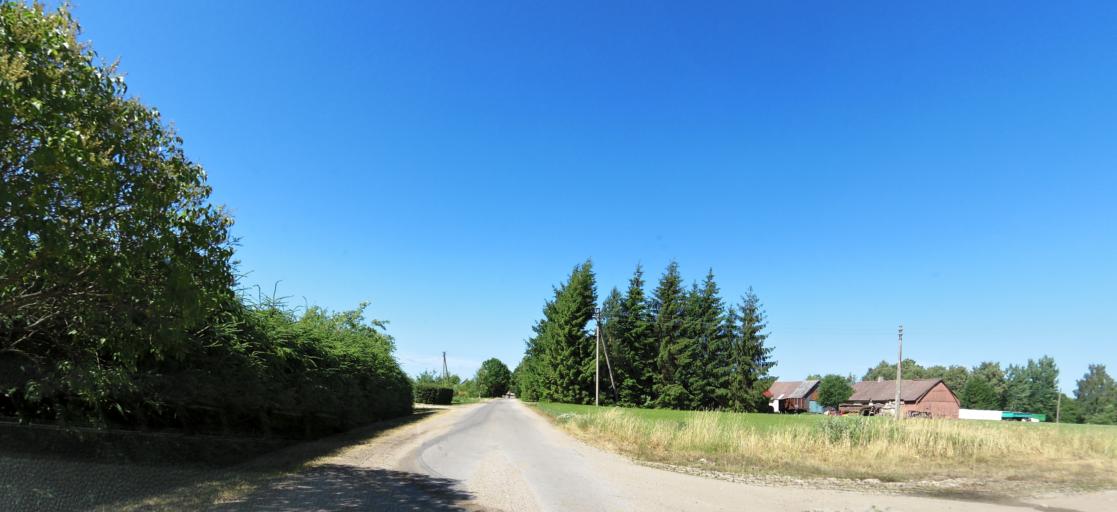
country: LT
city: Vabalninkas
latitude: 55.9732
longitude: 24.6617
